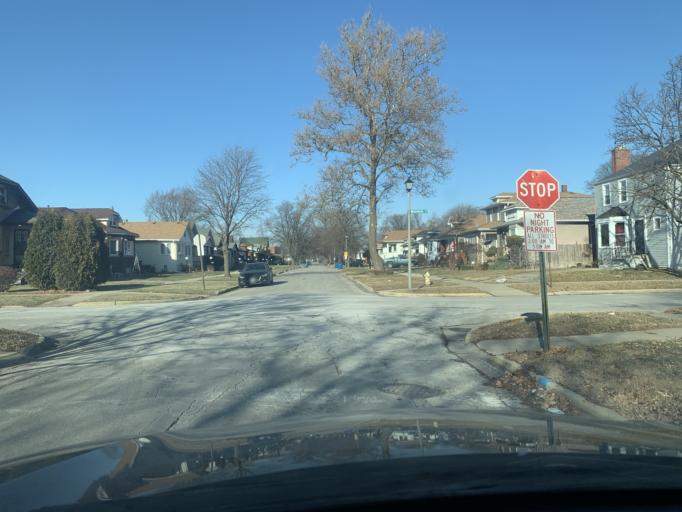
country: US
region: Illinois
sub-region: Cook County
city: Maywood
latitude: 41.8679
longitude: -87.8372
